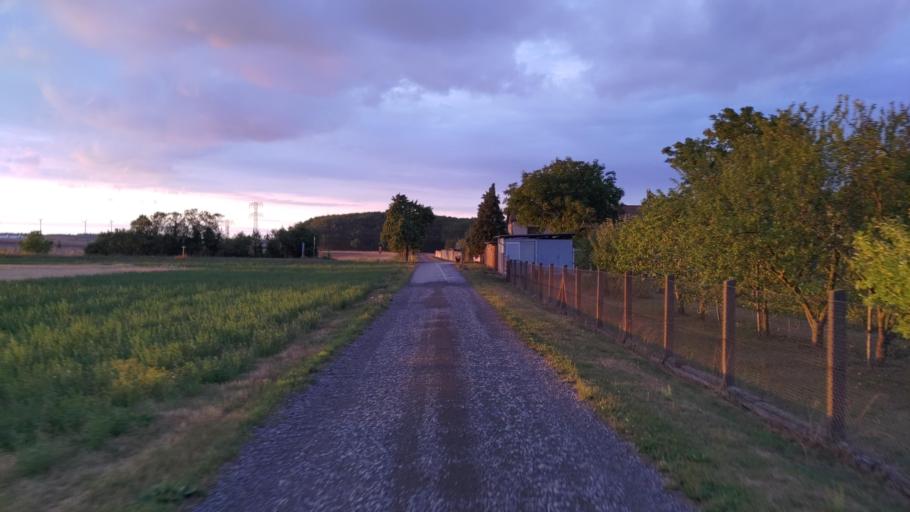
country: DE
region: Thuringia
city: Kleinmolsen
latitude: 50.9881
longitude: 11.1007
